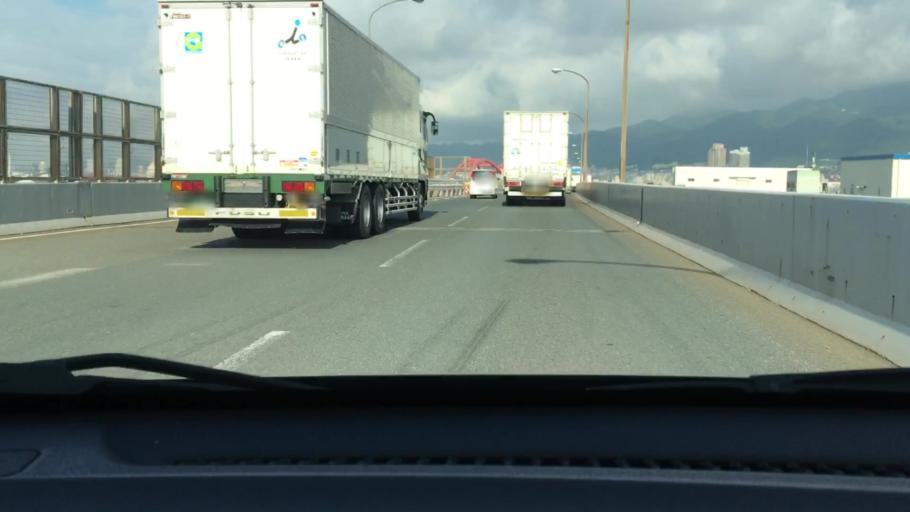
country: JP
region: Hyogo
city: Ashiya
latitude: 34.7060
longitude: 135.2636
